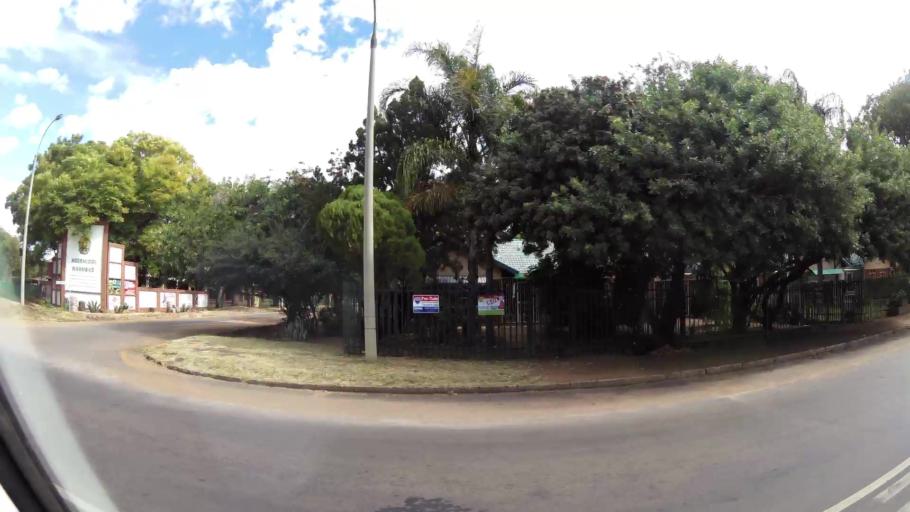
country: ZA
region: Limpopo
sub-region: Waterberg District Municipality
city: Warmbaths
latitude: -24.8875
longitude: 28.2845
